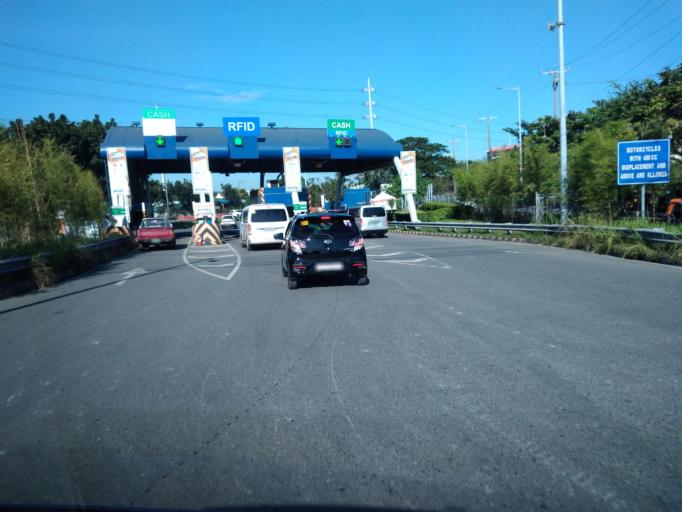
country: PH
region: Central Luzon
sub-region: Province of Bulacan
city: Meycauayan
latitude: 14.7476
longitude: 120.9728
